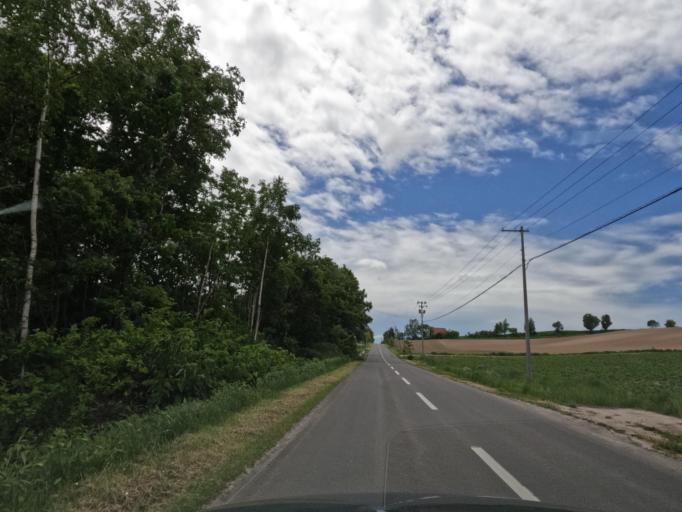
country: JP
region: Hokkaido
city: Shimo-furano
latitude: 43.5246
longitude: 142.4341
